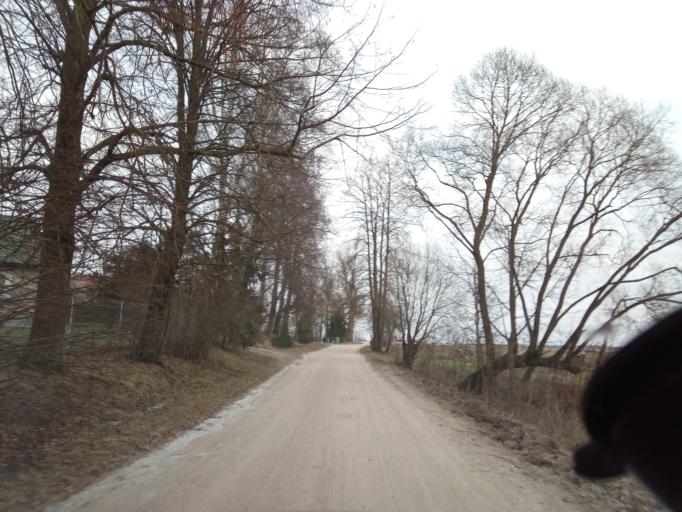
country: LT
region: Alytaus apskritis
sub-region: Alytaus rajonas
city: Daugai
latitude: 54.3677
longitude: 24.4472
